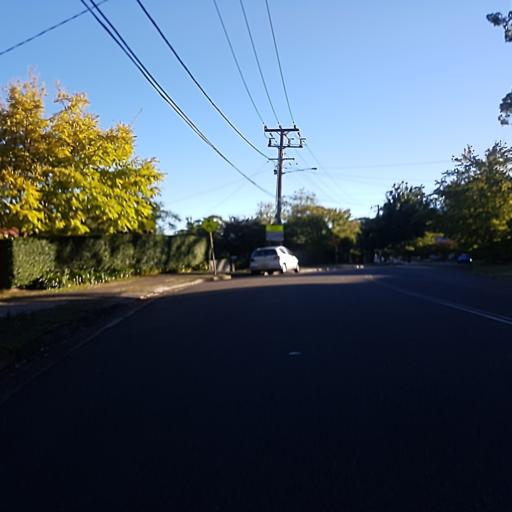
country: AU
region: New South Wales
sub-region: Warringah
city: Davidson
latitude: -33.7421
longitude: 151.2084
